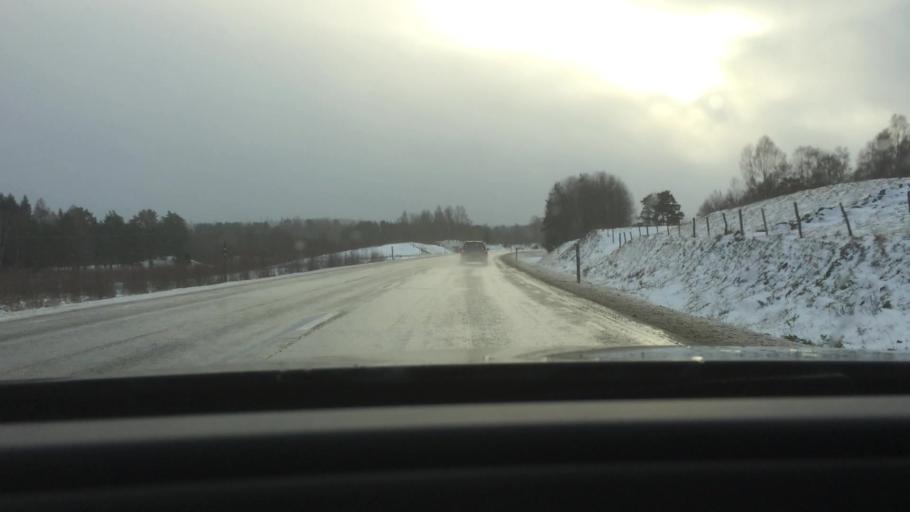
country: SE
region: Vaestra Goetaland
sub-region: Falkopings Kommun
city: Falkoeping
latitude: 57.9740
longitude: 13.5293
